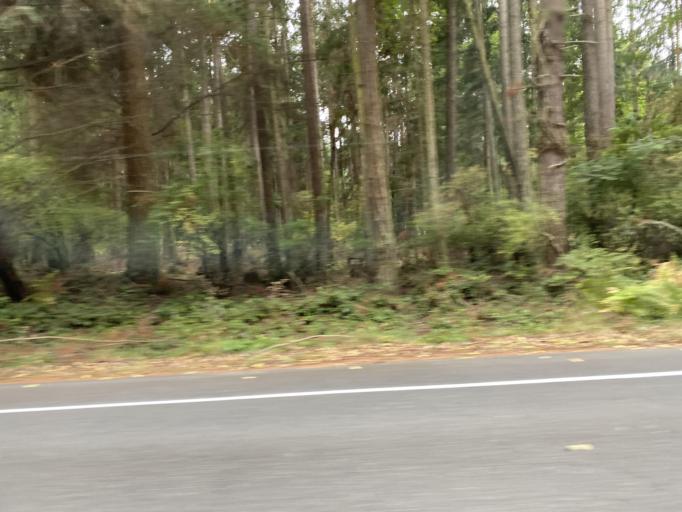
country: US
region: Washington
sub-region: Island County
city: Coupeville
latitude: 48.2146
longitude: -122.6345
